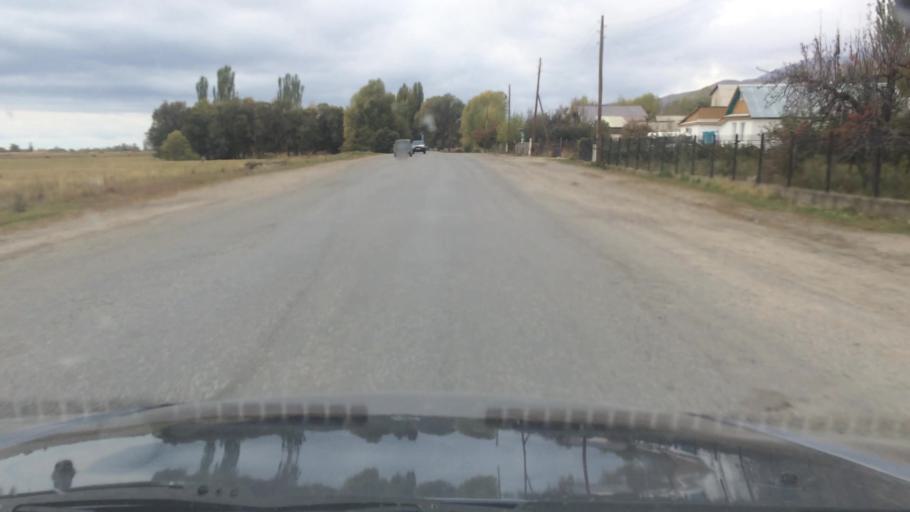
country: KG
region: Ysyk-Koel
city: Tyup
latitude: 42.7782
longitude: 78.2098
